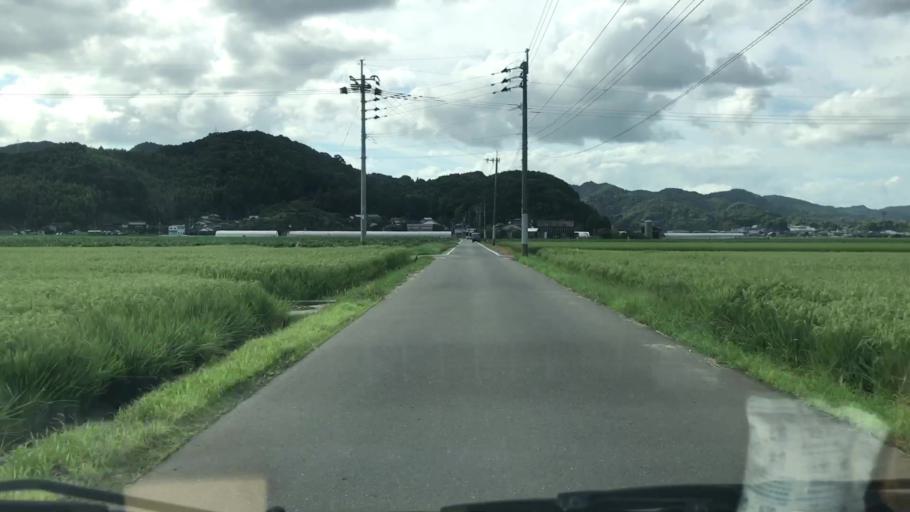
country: JP
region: Saga Prefecture
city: Kashima
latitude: 33.1158
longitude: 130.0762
